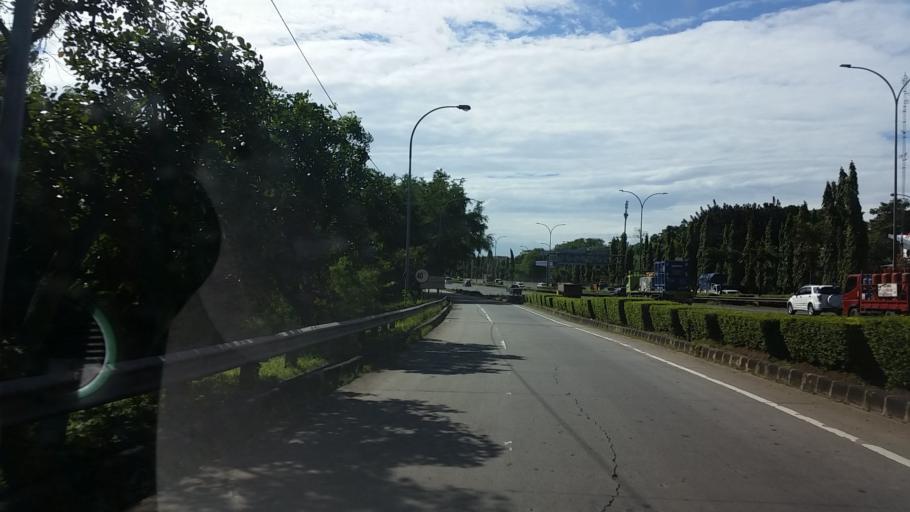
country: ID
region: Banten
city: South Tangerang
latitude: -6.2749
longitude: 106.7680
